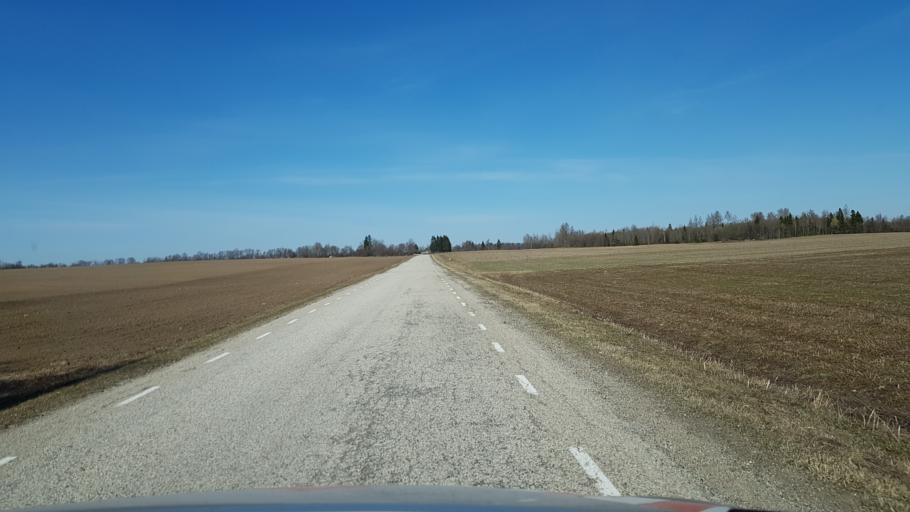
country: EE
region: Laeaene-Virumaa
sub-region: Vinni vald
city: Vinni
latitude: 59.0801
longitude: 26.5478
